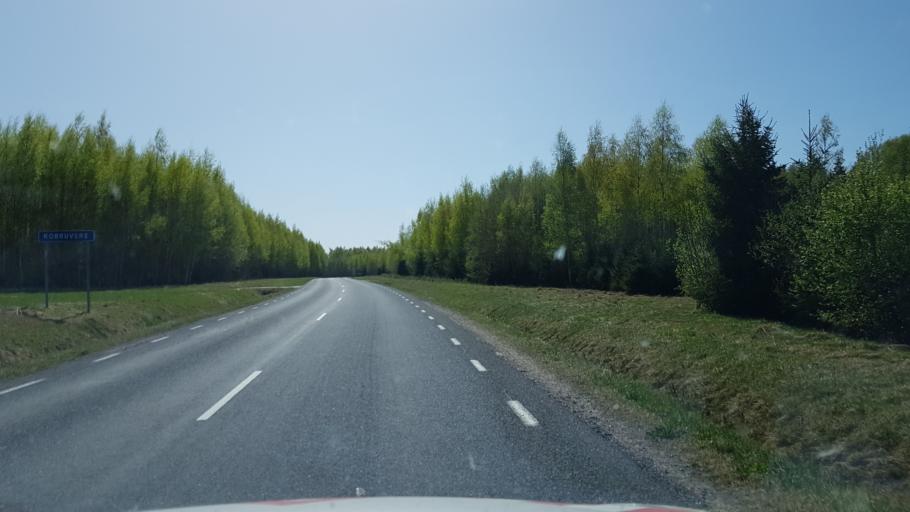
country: EE
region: Viljandimaa
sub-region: Suure-Jaani vald
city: Suure-Jaani
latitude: 58.4865
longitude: 25.4449
